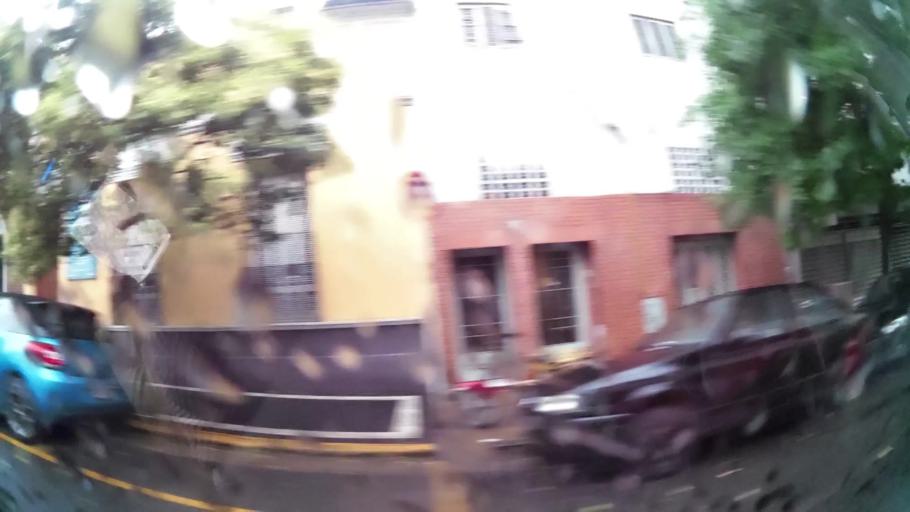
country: AR
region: Buenos Aires F.D.
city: Buenos Aires
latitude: -34.6291
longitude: -58.3741
